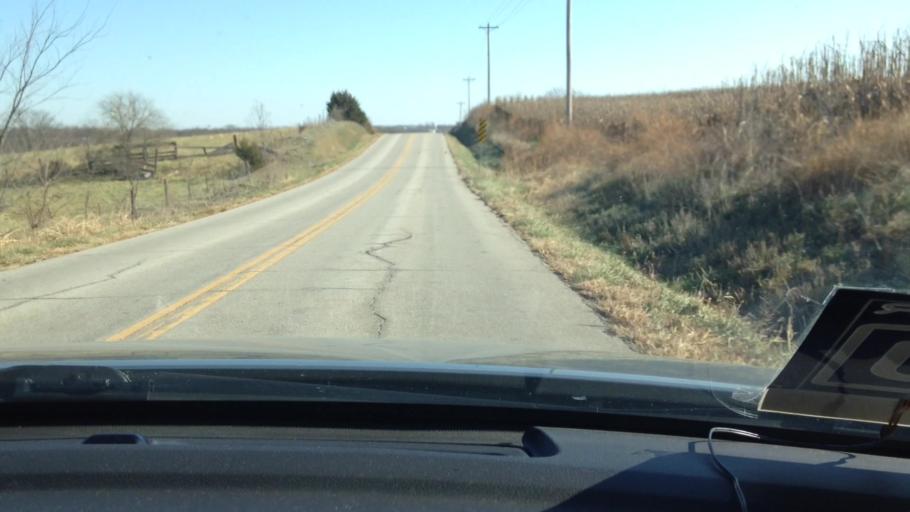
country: US
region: Missouri
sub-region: Platte County
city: Weston
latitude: 39.4981
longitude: -94.8235
